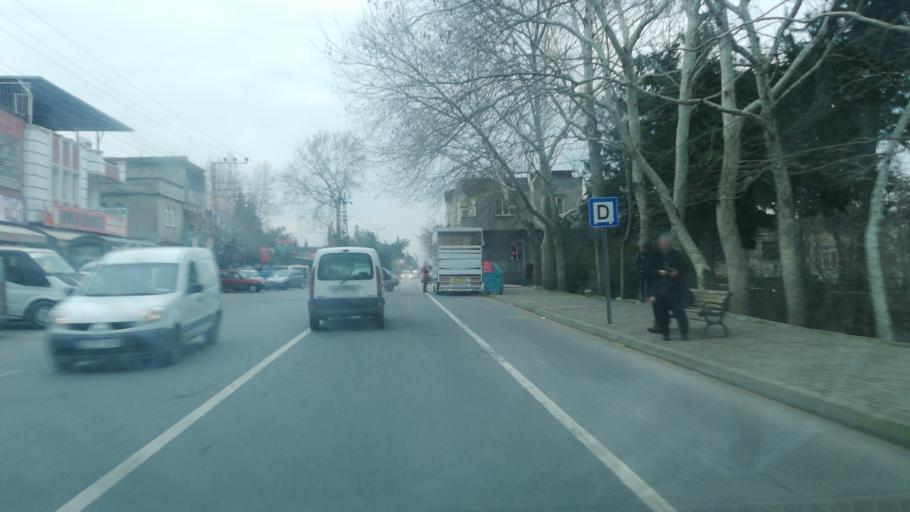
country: TR
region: Kahramanmaras
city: Kahramanmaras
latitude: 37.5714
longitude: 36.9463
